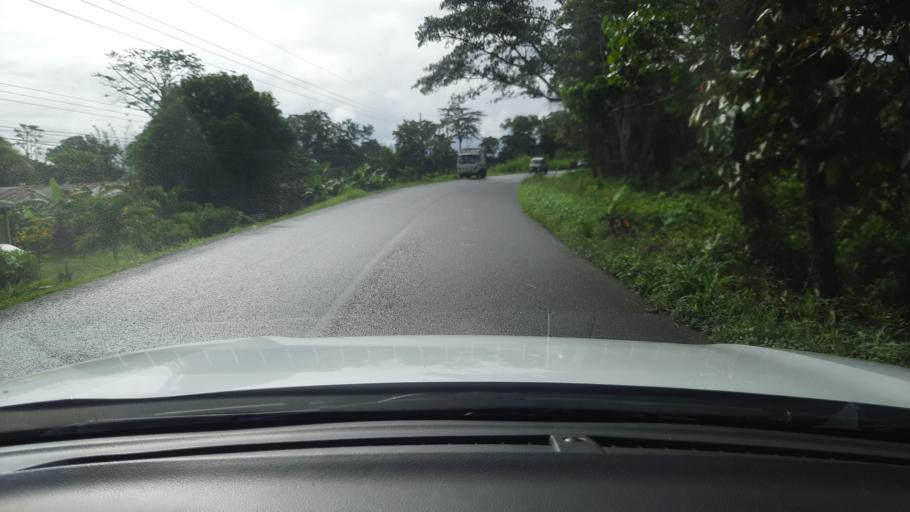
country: CR
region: Alajuela
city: San Jose
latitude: 10.9351
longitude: -85.1045
